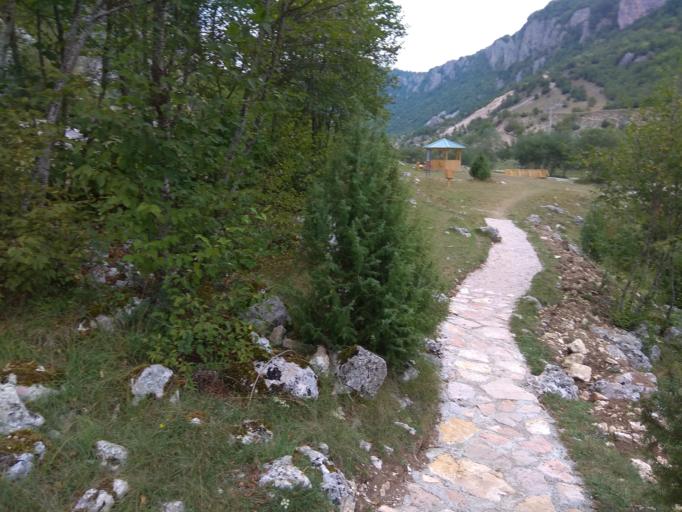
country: ME
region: Opstina Savnik
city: Savnik
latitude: 42.9889
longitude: 19.0678
